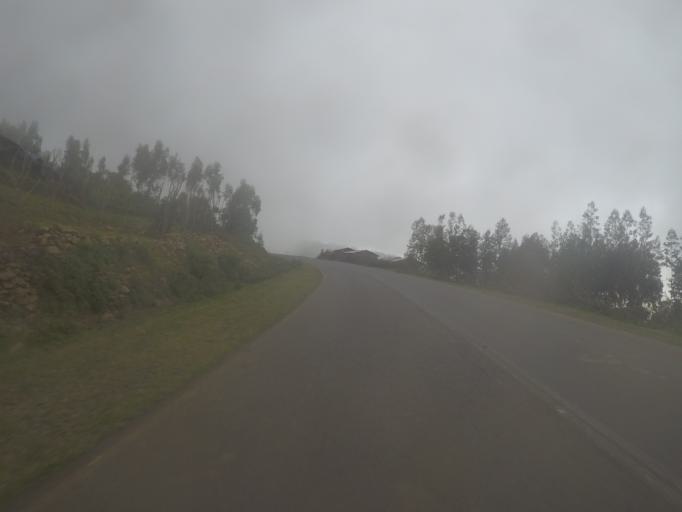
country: ET
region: Amhara
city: Gondar
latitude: 12.7427
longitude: 37.5188
